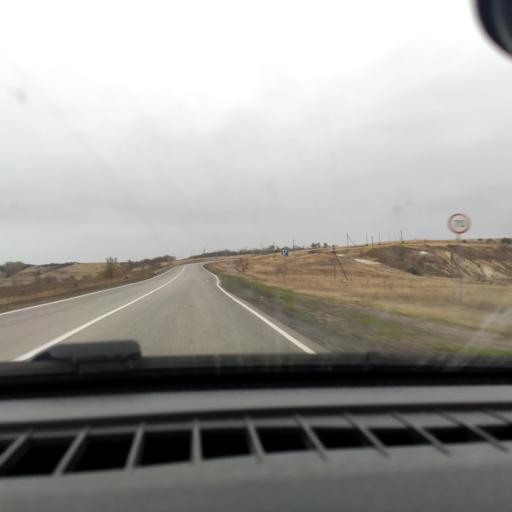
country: RU
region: Voronezj
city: Uryv-Pokrovka
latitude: 51.1329
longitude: 39.0459
